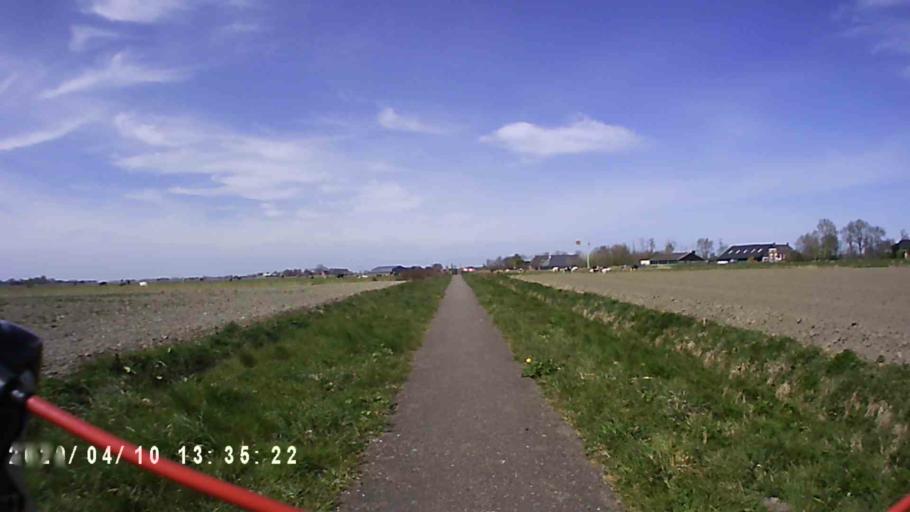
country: NL
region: Groningen
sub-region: Gemeente Zuidhorn
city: Oldehove
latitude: 53.3701
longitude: 6.4022
